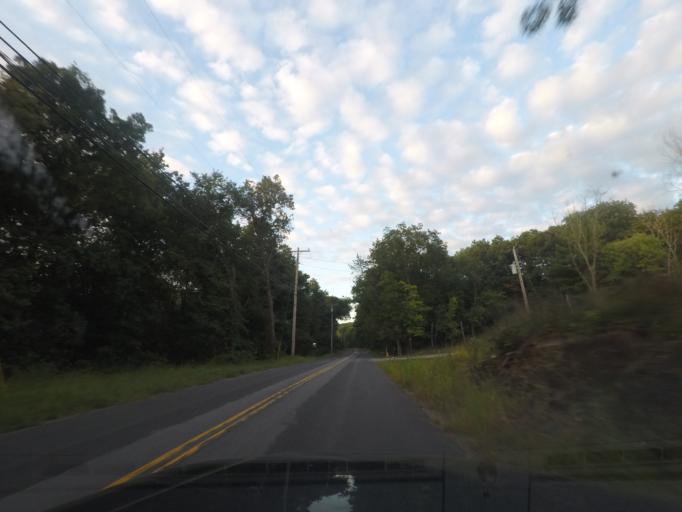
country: US
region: New York
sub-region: Rensselaer County
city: Nassau
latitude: 42.5233
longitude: -73.6048
